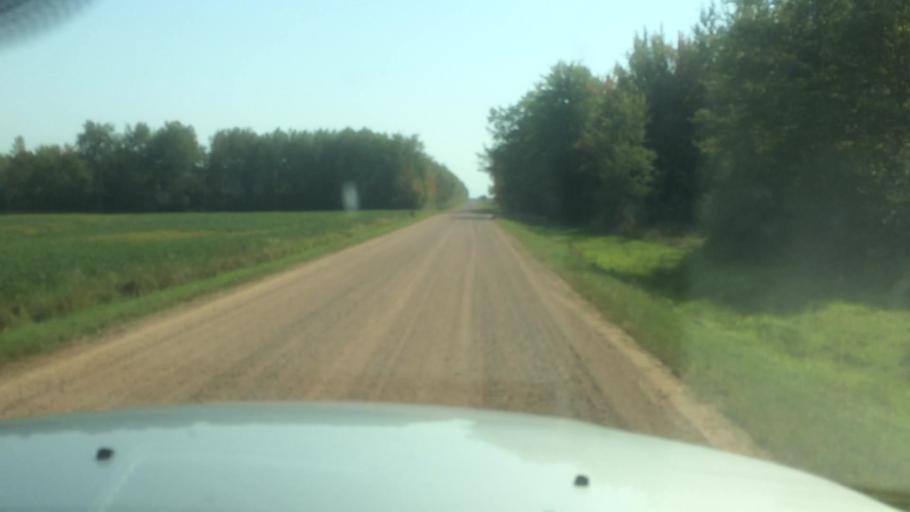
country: US
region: Wisconsin
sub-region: Taylor County
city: Medford
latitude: 45.0907
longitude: -90.2793
